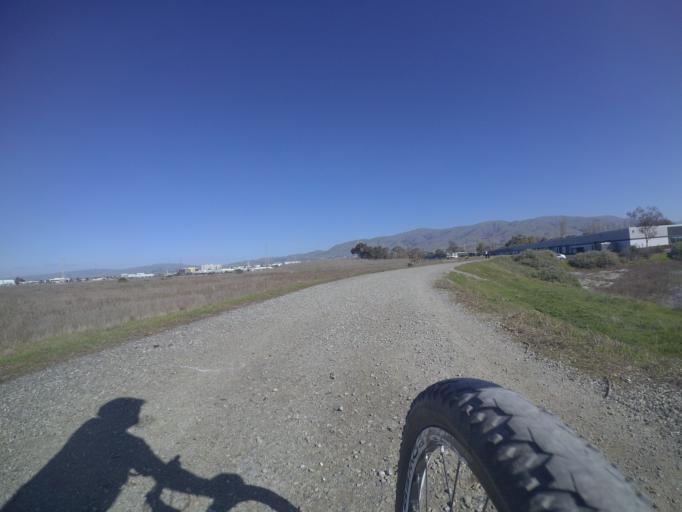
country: US
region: California
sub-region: Santa Clara County
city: Milpitas
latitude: 37.4791
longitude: -121.9504
